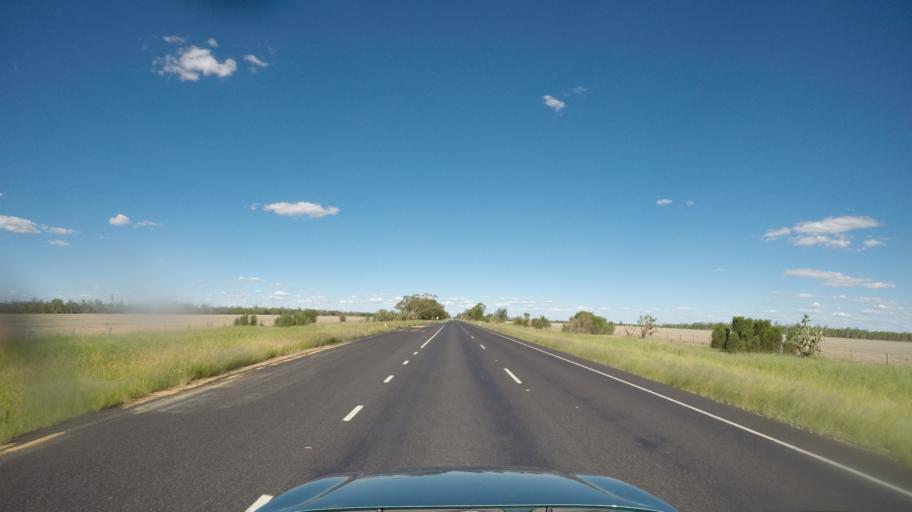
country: AU
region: Queensland
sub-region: Goondiwindi
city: Goondiwindi
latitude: -28.1764
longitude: 150.4788
